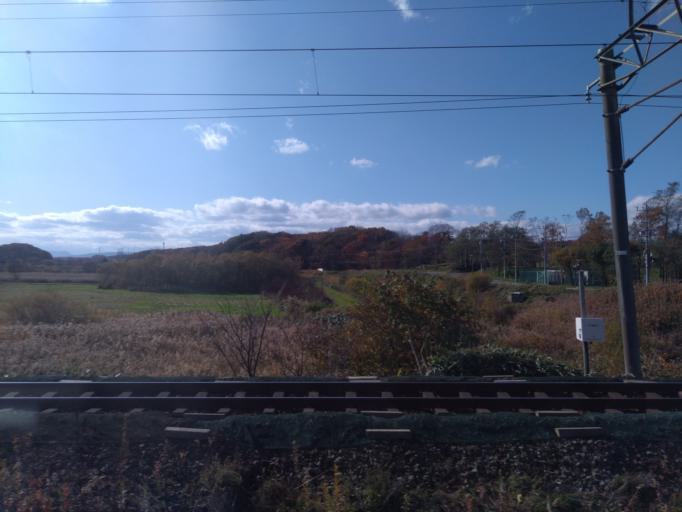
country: JP
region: Hokkaido
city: Kitahiroshima
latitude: 42.9677
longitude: 141.5668
